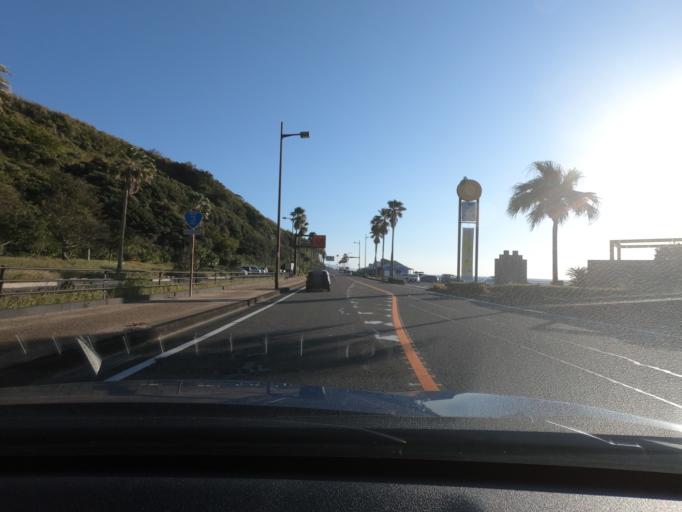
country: JP
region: Kagoshima
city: Akune
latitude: 31.9470
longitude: 130.2168
